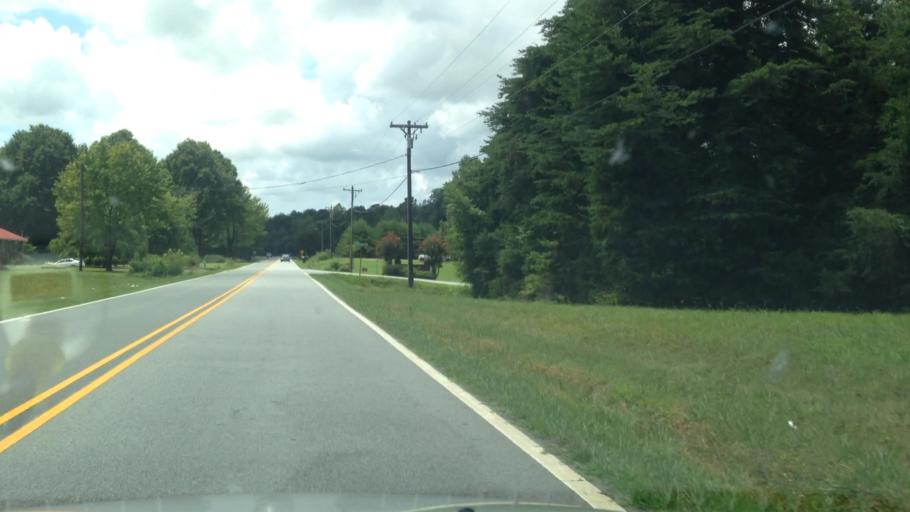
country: US
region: North Carolina
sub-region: Forsyth County
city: Walkertown
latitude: 36.1585
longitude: -80.1193
